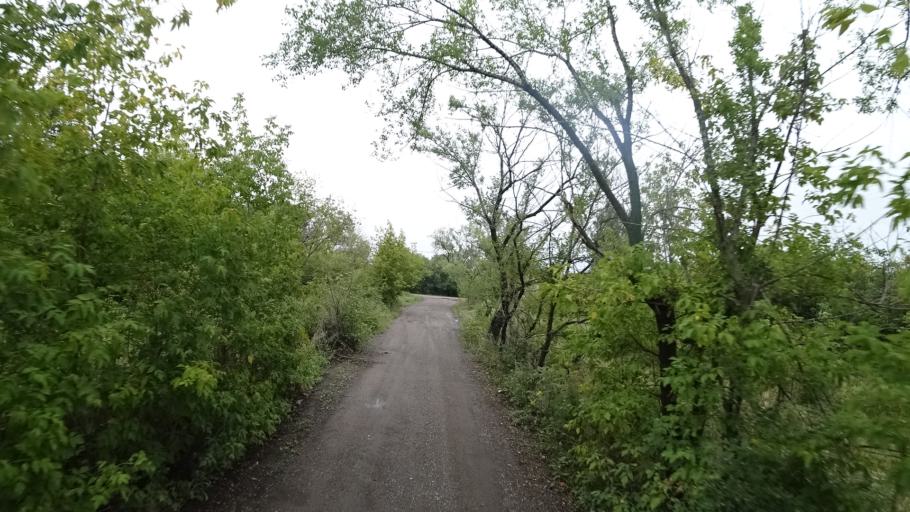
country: RU
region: Primorskiy
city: Chernigovka
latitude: 44.3307
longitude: 132.6014
